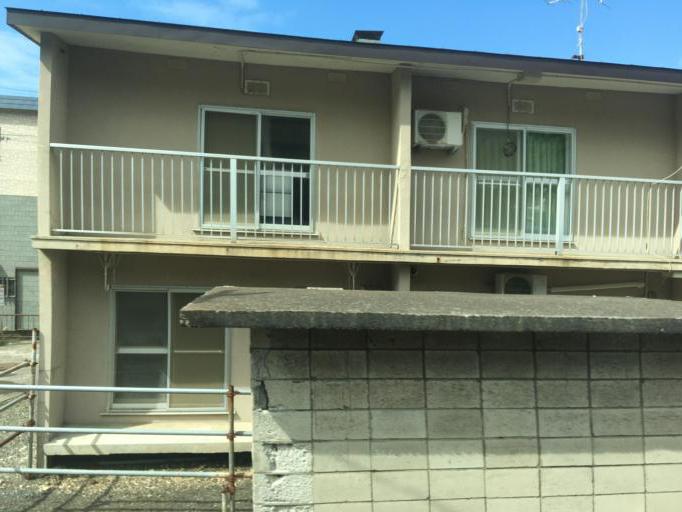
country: JP
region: Akita
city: Noshiromachi
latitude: 40.6497
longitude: 139.9289
